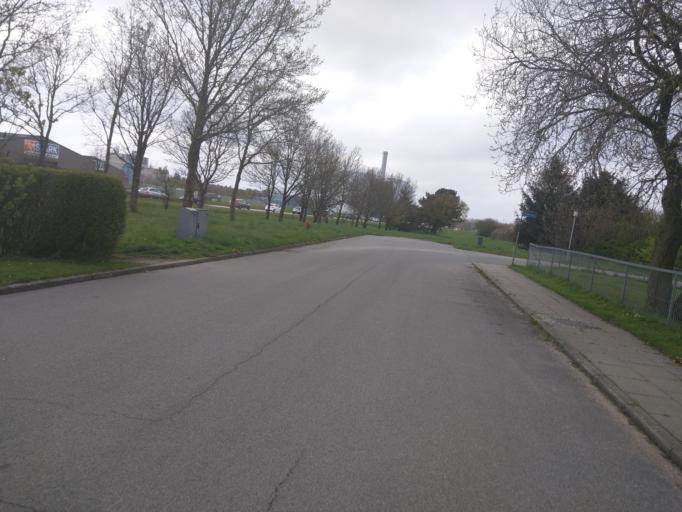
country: DK
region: Central Jutland
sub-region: Viborg Kommune
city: Viborg
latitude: 56.4701
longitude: 9.4158
